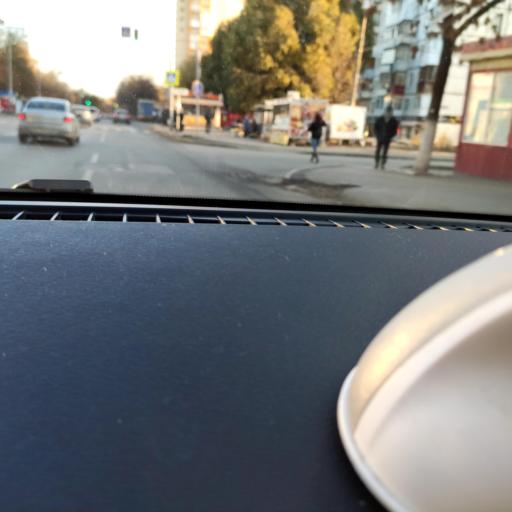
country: RU
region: Samara
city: Samara
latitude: 53.2517
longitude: 50.2372
